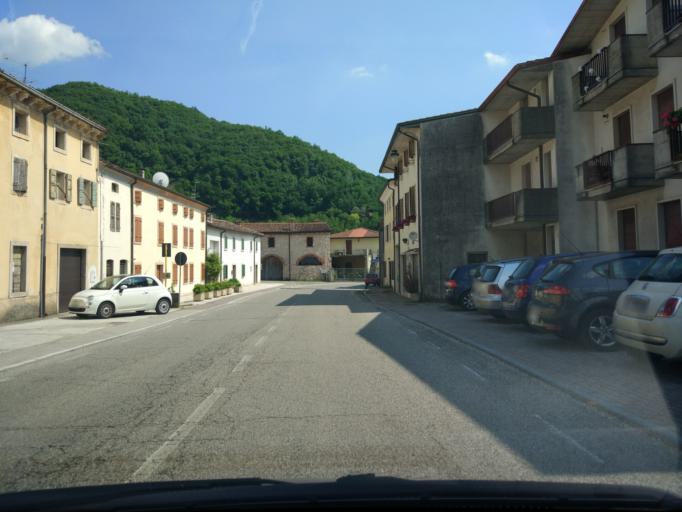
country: IT
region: Veneto
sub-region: Provincia di Verona
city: Badia Calavena
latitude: 45.5631
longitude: 11.1544
